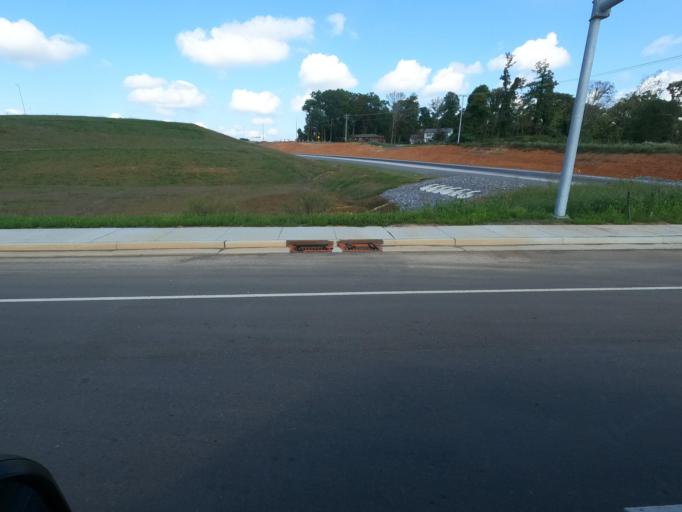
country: US
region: Tennessee
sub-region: Blount County
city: Alcoa
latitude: 35.7979
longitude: -83.9893
